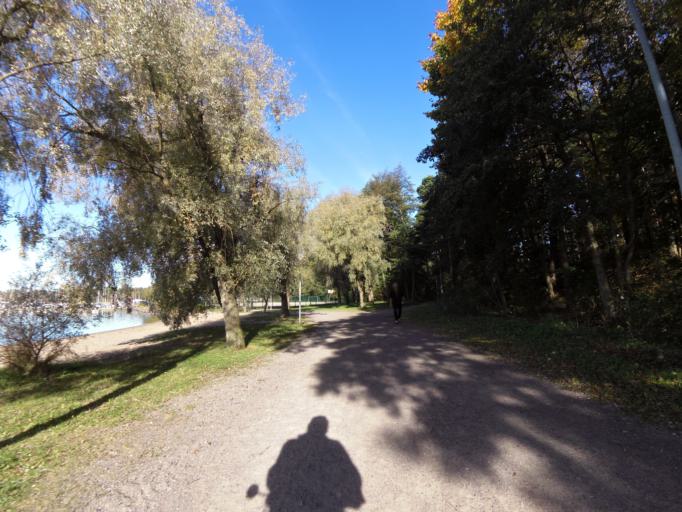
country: FI
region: Uusimaa
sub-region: Helsinki
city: Espoo
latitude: 60.1537
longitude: 24.6263
